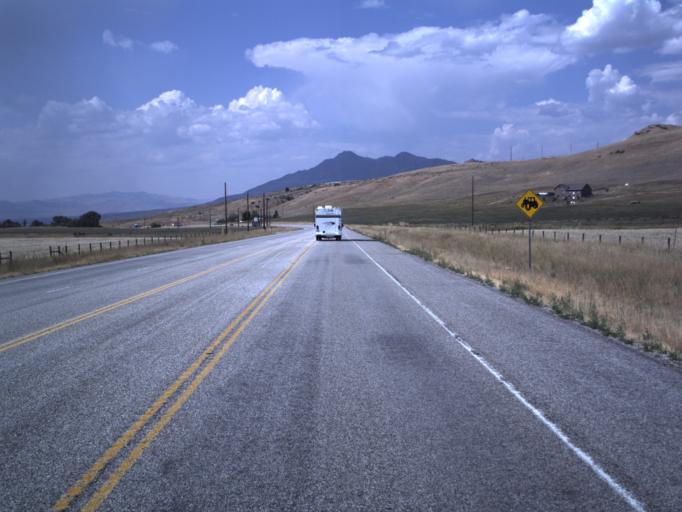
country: US
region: Utah
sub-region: Cache County
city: Mendon
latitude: 41.7878
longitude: -112.0287
